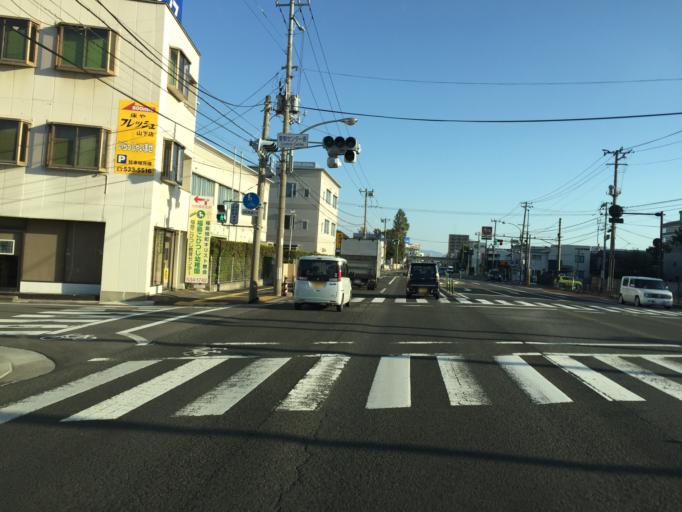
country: JP
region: Fukushima
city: Fukushima-shi
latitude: 37.7641
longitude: 140.4778
